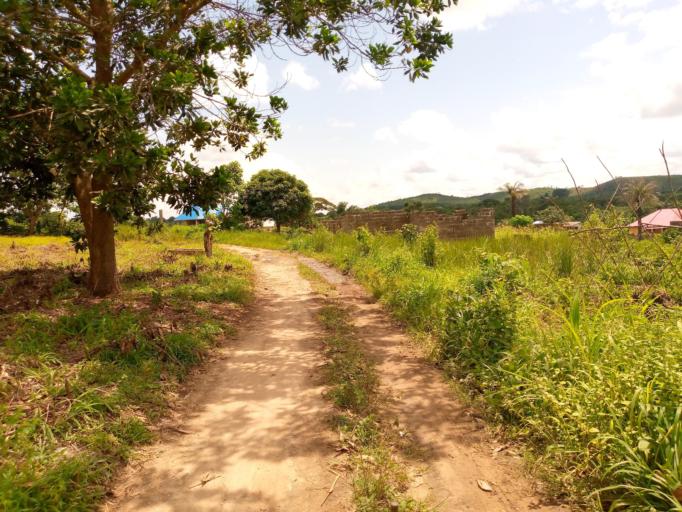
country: SL
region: Northern Province
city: Magburaka
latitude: 8.7323
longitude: -11.9396
